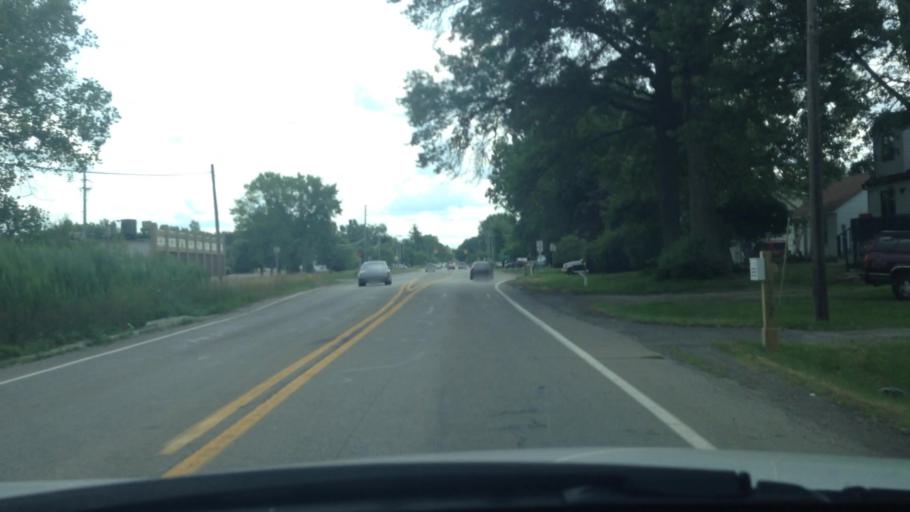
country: US
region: Michigan
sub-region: Wayne County
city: Taylor
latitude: 42.1991
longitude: -83.3067
